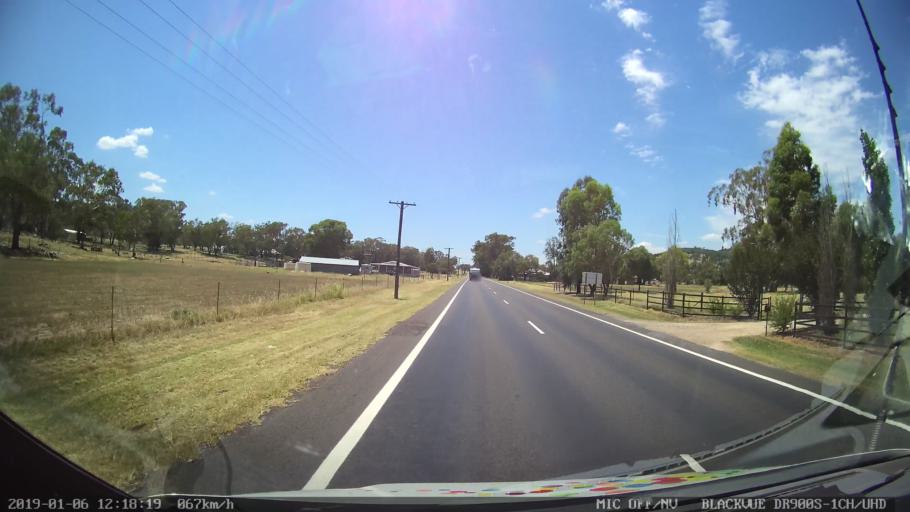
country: AU
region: New South Wales
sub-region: Tamworth Municipality
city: Phillip
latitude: -31.2632
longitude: 150.7422
